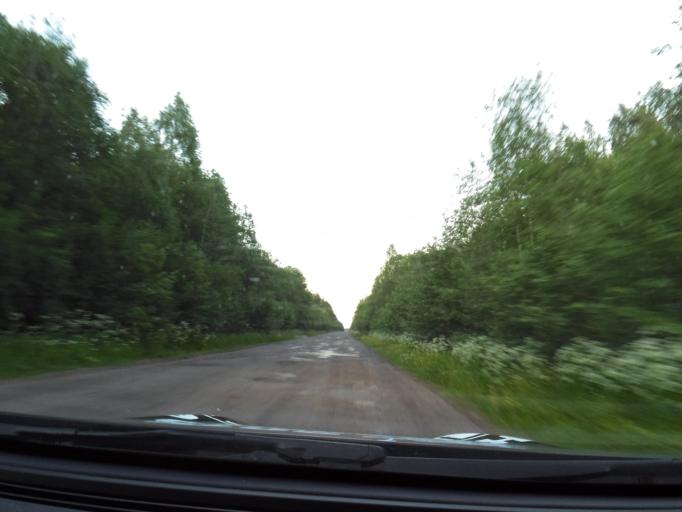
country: RU
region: Leningrad
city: Voznesen'ye
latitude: 60.8309
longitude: 35.6909
